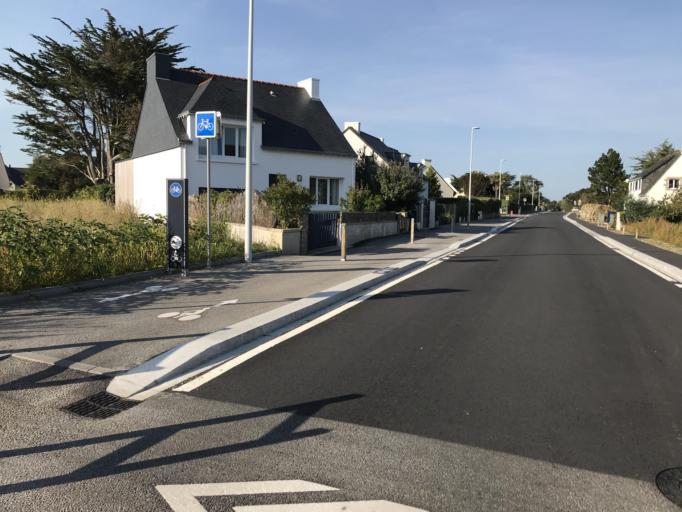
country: FR
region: Brittany
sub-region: Departement du Morbihan
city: Arzon
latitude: 47.5487
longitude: -2.9009
